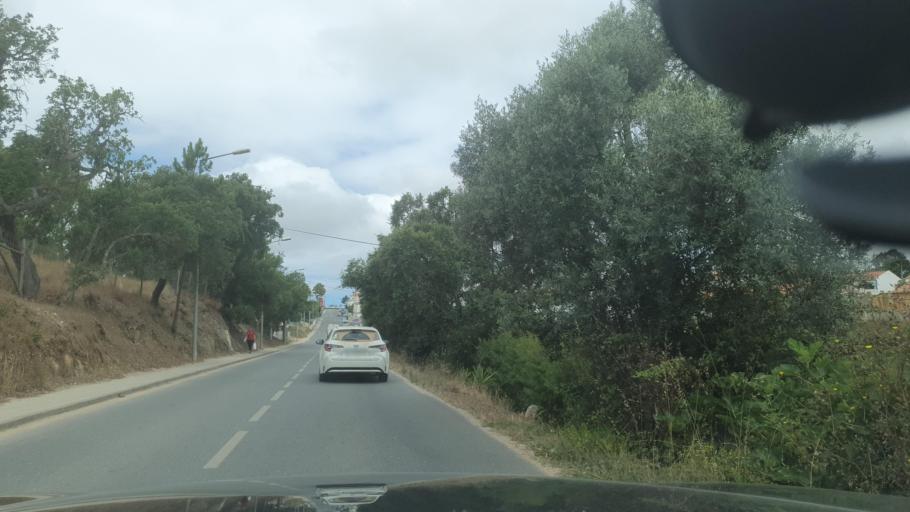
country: PT
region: Beja
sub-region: Odemira
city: Sao Teotonio
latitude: 37.5098
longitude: -8.7123
